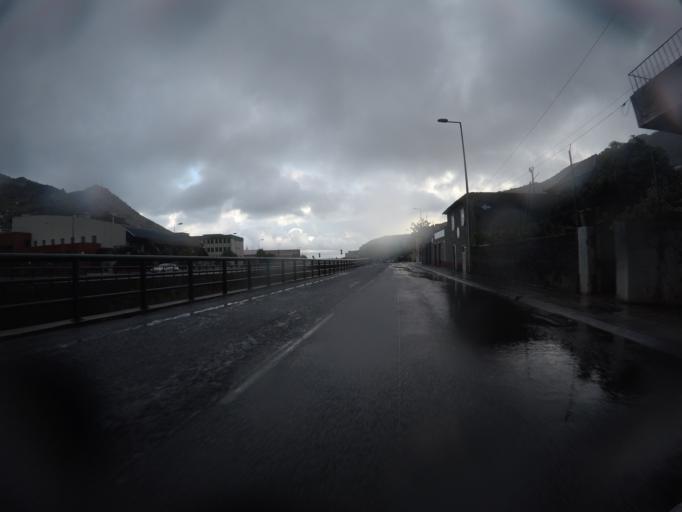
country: PT
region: Madeira
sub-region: Machico
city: Machico
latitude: 32.7266
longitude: -16.7726
